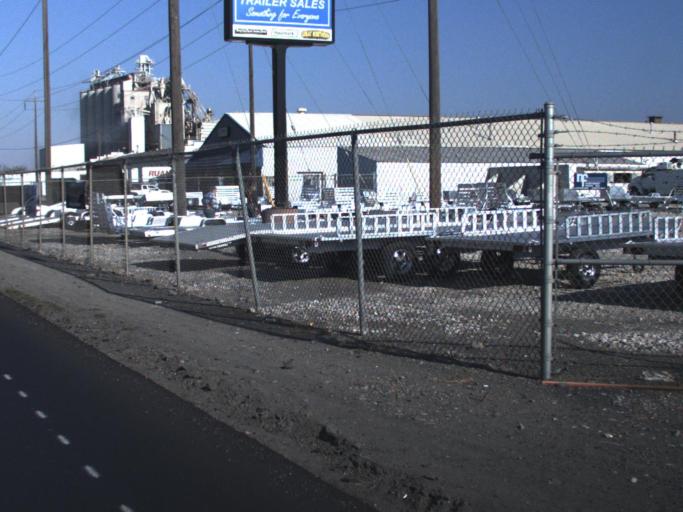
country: US
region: Washington
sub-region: Spokane County
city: Millwood
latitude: 47.6723
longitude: -117.3422
